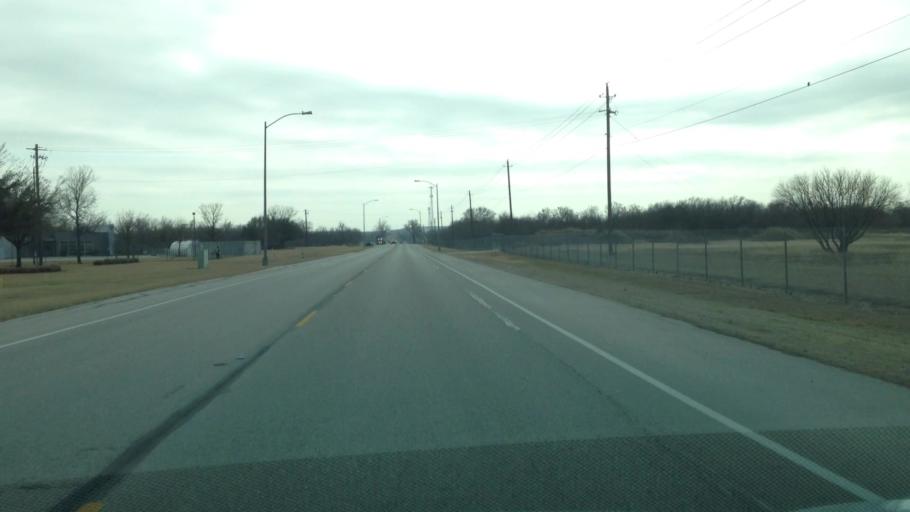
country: US
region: Texas
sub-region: Travis County
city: Hornsby Bend
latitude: 30.1839
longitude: -97.6643
